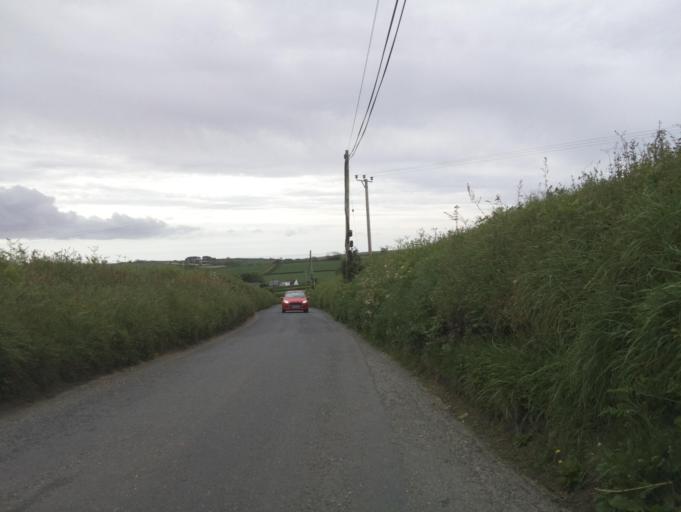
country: GB
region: England
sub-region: Devon
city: Dartmouth
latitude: 50.3503
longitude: -3.6598
